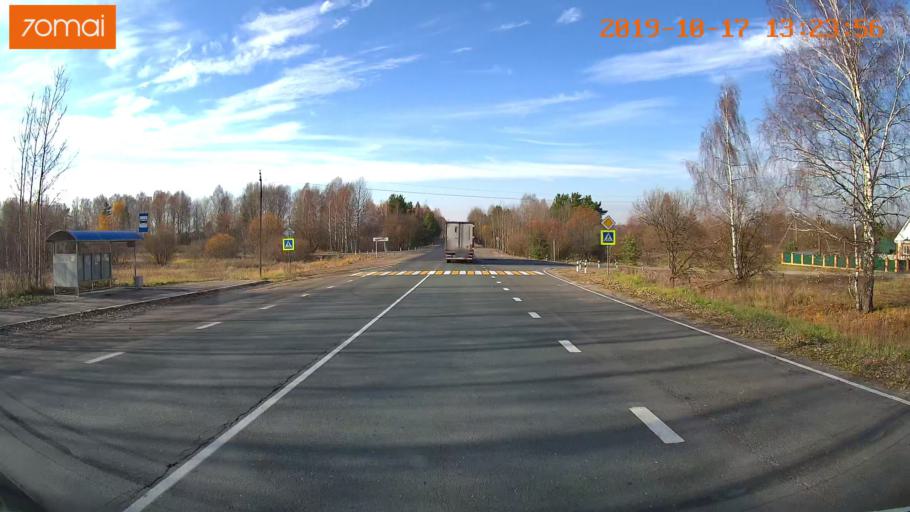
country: RU
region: Rjazan
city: Gus'-Zheleznyy
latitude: 55.0923
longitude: 40.9718
